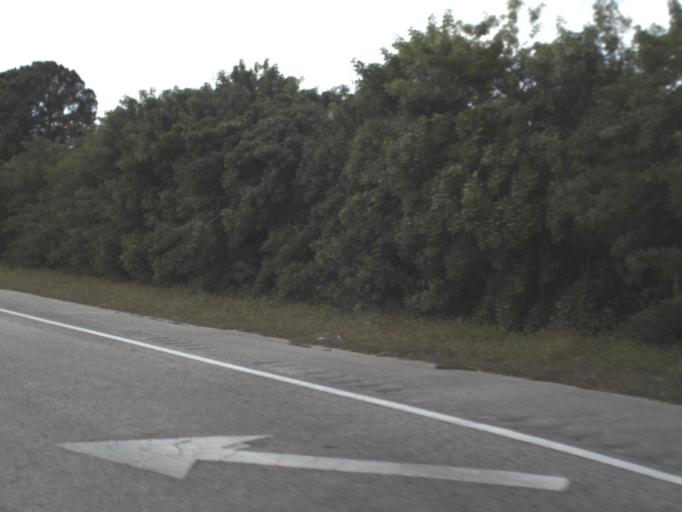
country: US
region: Florida
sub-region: Brevard County
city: Cocoa
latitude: 28.4002
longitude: -80.7590
